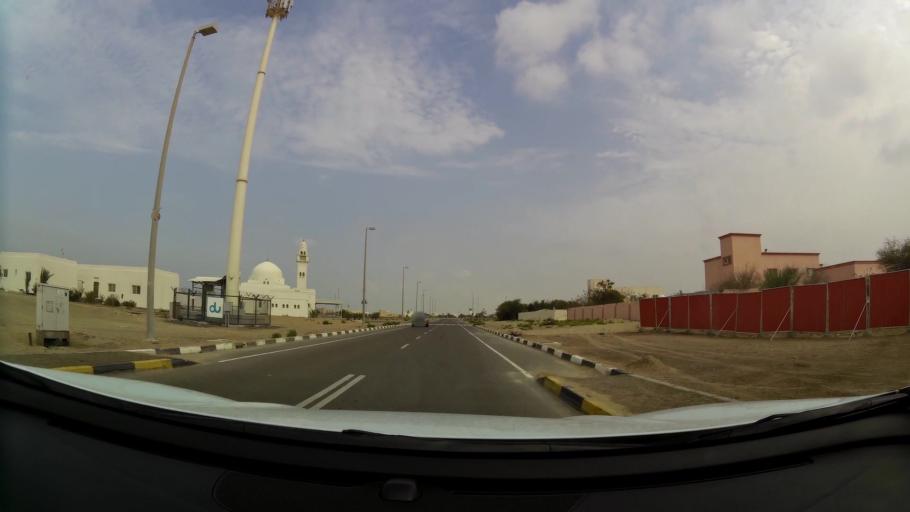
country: AE
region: Abu Dhabi
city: Abu Dhabi
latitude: 24.6354
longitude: 54.6712
